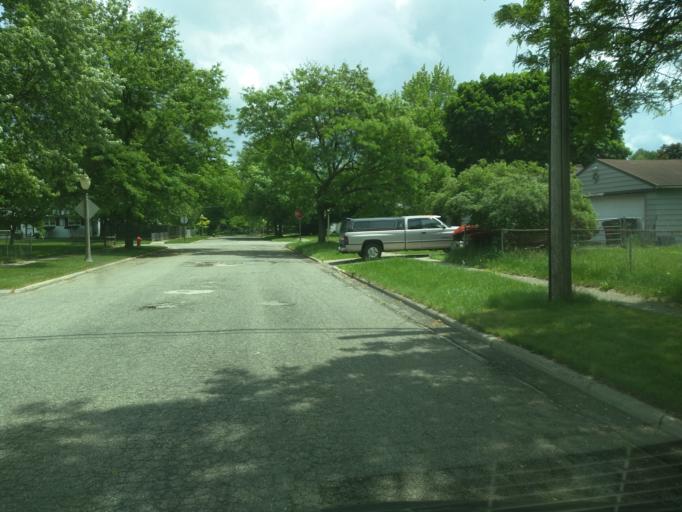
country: US
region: Michigan
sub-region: Eaton County
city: Waverly
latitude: 42.6964
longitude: -84.5950
